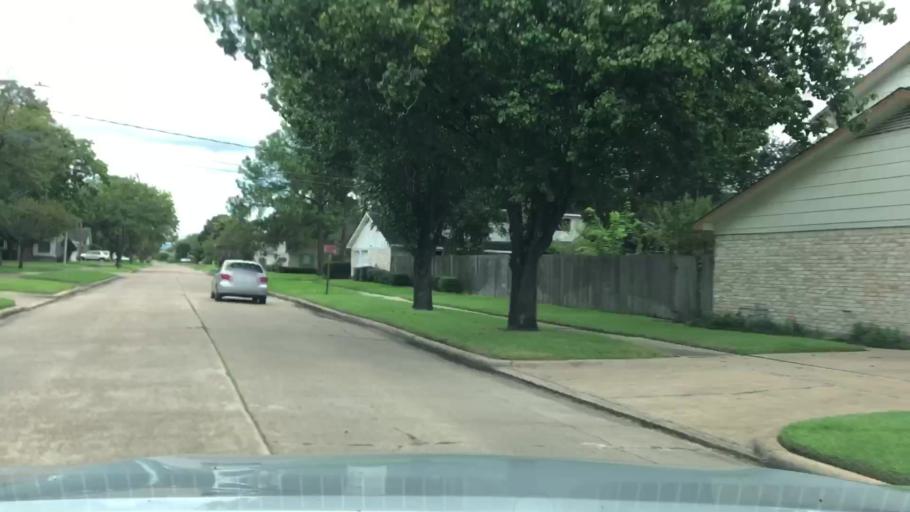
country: US
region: Texas
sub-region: Fort Bend County
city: Meadows Place
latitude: 29.7006
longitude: -95.5472
